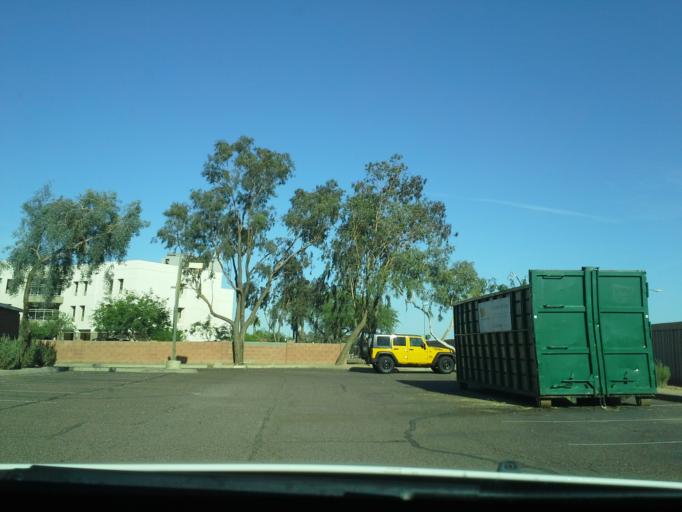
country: US
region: Arizona
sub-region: Maricopa County
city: Phoenix
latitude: 33.4629
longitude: -112.0631
